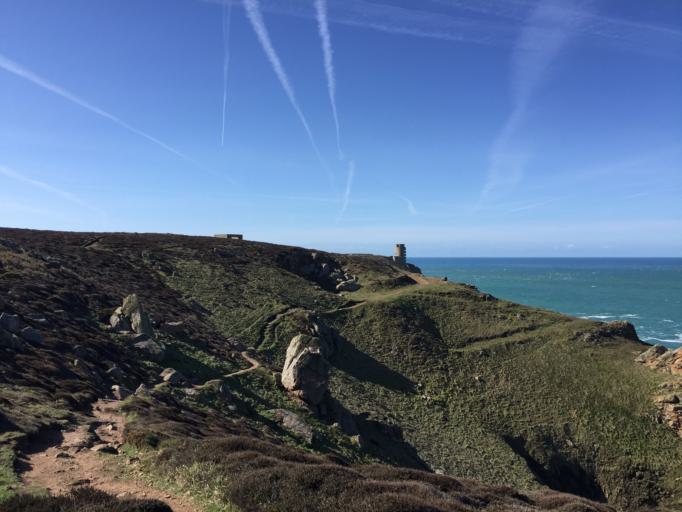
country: JE
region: St Helier
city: Saint Helier
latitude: 49.2553
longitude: -2.2487
